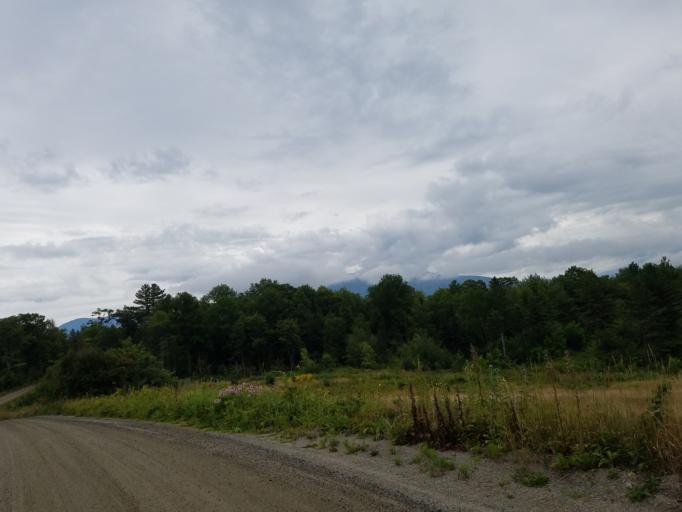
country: US
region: New Hampshire
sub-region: Coos County
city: Lancaster
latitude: 44.4418
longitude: -71.5713
